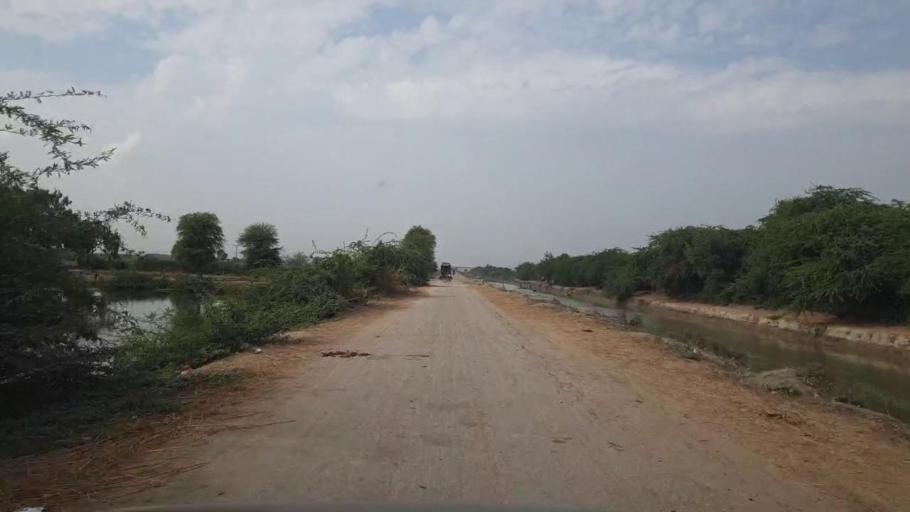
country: PK
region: Sindh
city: Kario
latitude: 24.6348
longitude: 68.5676
